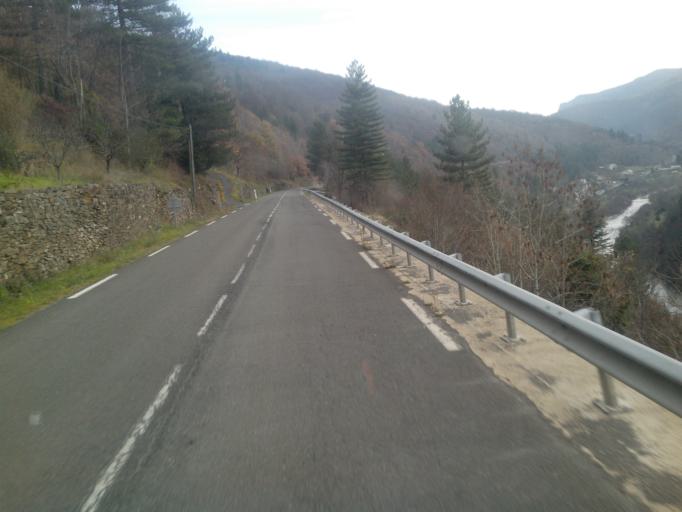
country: FR
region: Languedoc-Roussillon
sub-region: Departement de la Lozere
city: Florac
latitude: 44.3766
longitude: 3.5530
